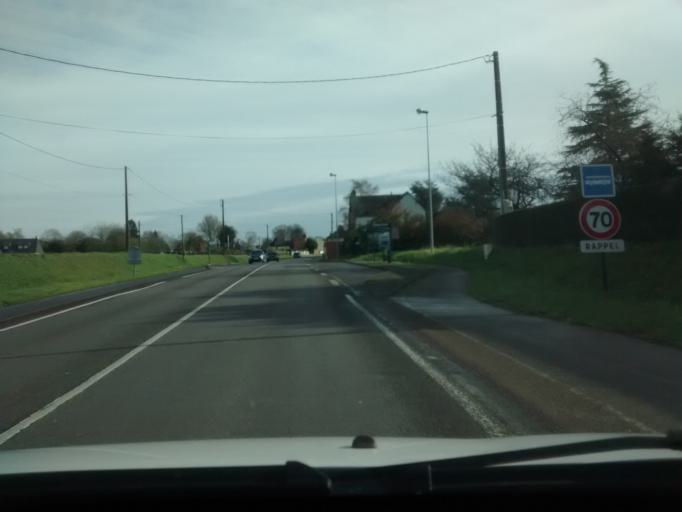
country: FR
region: Brittany
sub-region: Departement d'Ille-et-Vilaine
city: Vezin-le-Coquet
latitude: 48.1177
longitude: -1.7324
